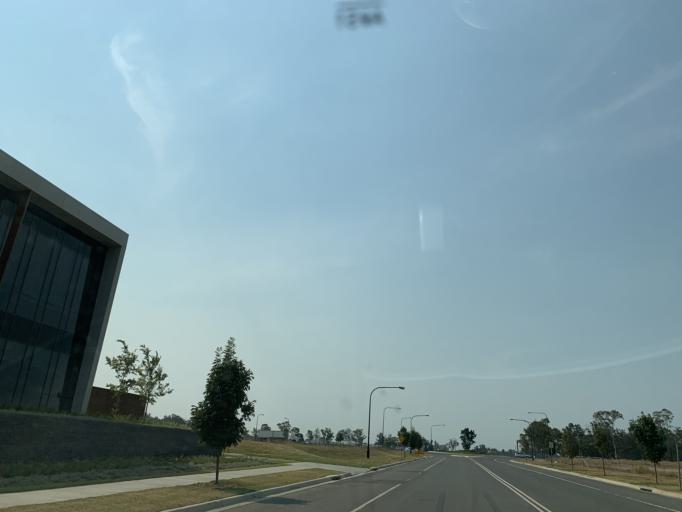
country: AU
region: New South Wales
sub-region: Blacktown
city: Hassall Grove
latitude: -33.7138
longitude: 150.8403
